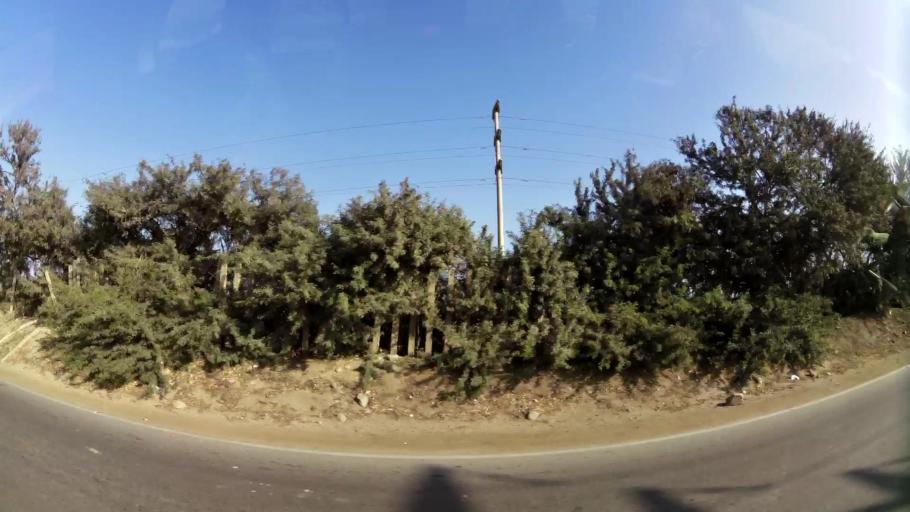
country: PE
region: Ica
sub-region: Provincia de Chincha
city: Chincha Baja
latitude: -13.4505
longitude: -76.1484
